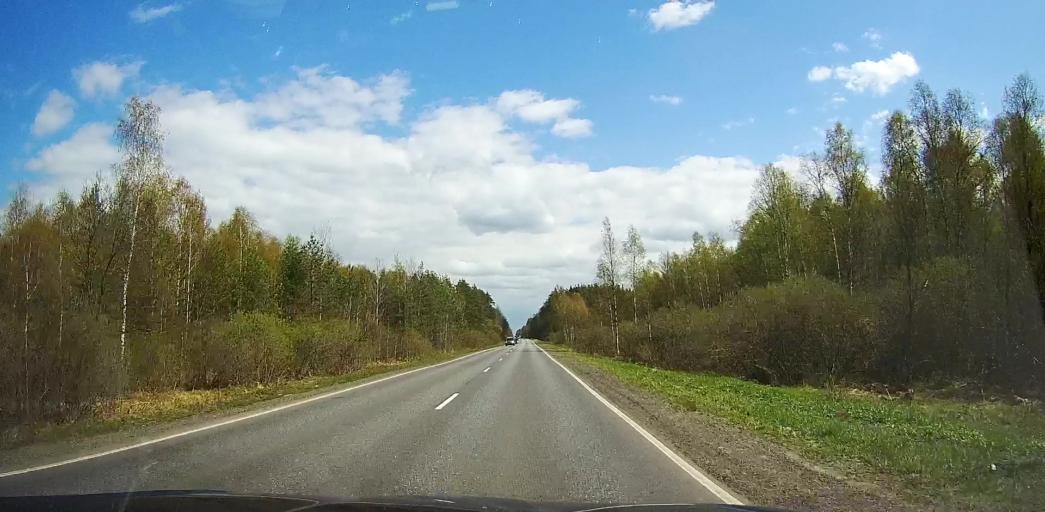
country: RU
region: Moskovskaya
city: Imeni Tsyurupy
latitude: 55.5514
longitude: 38.7187
